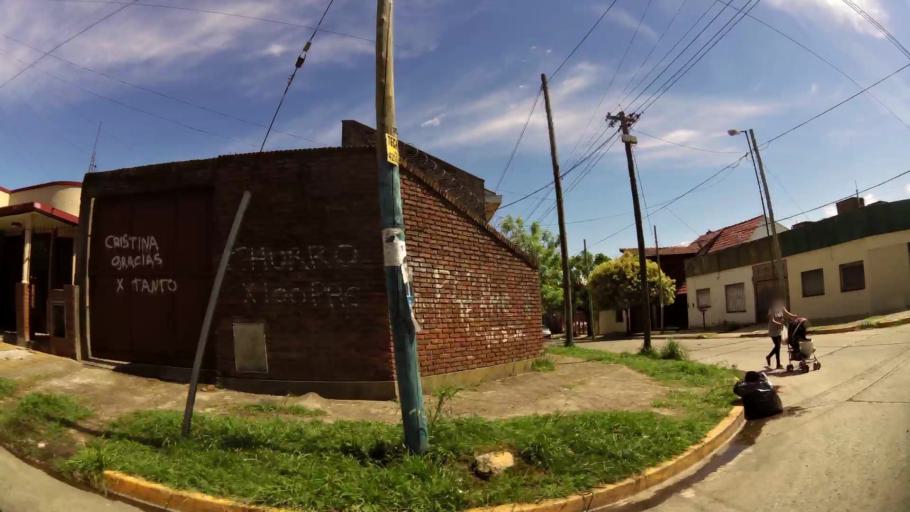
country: AR
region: Buenos Aires
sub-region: Partido de Quilmes
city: Quilmes
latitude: -34.7128
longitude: -58.2592
